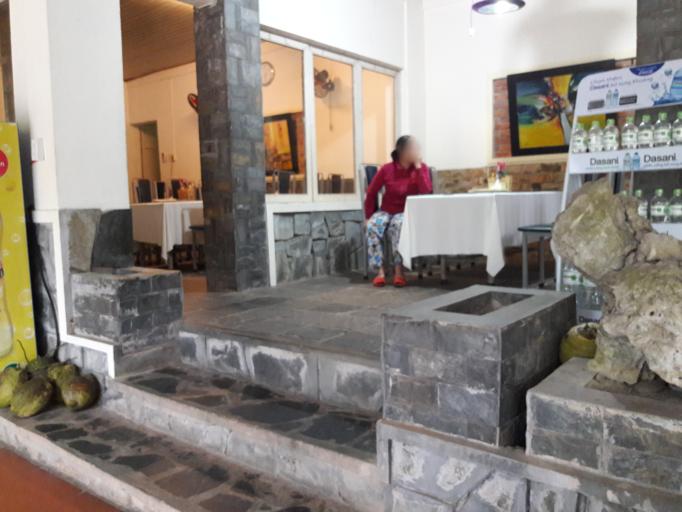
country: VN
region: Thua Thien-Hue
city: Hue
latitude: 16.4309
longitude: 107.5660
